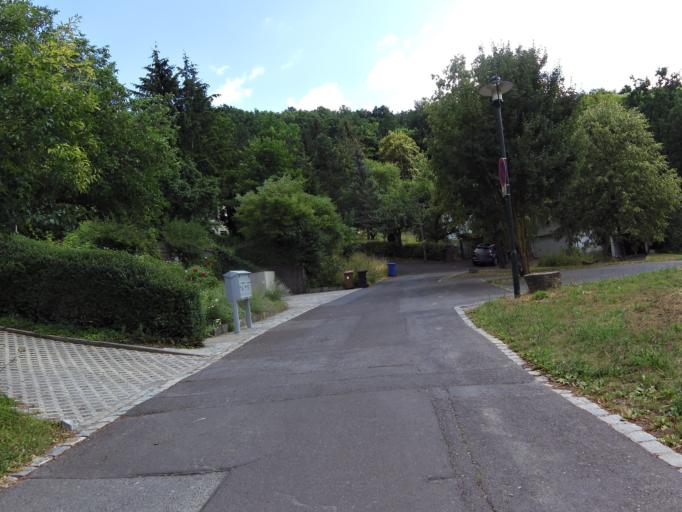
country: DE
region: Bavaria
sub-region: Regierungsbezirk Unterfranken
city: Gerbrunn
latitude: 49.7841
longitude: 9.9984
